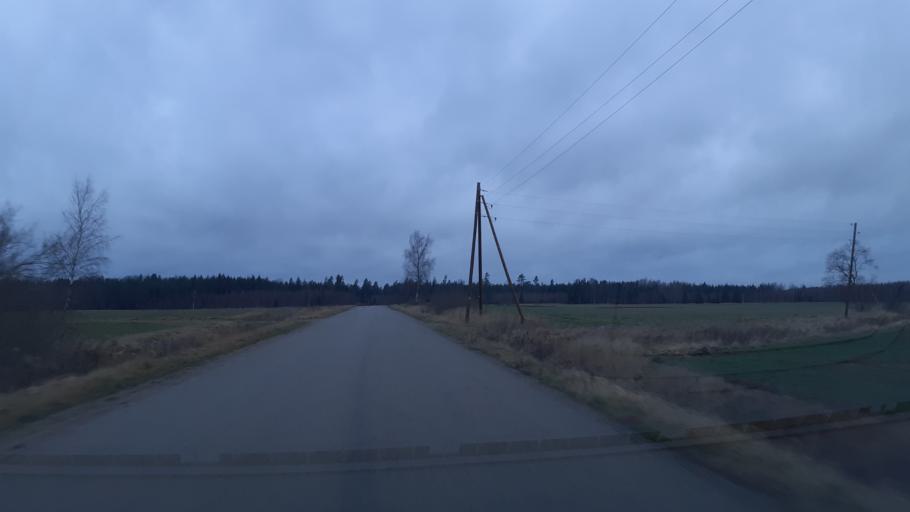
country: LV
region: Kuldigas Rajons
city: Kuldiga
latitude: 57.0272
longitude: 22.1641
